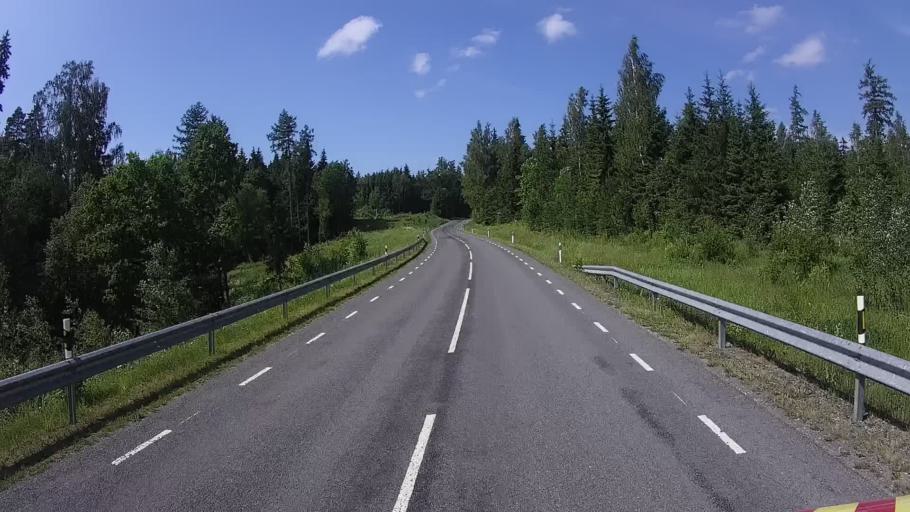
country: EE
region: Viljandimaa
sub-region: Karksi vald
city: Karksi-Nuia
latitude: 58.0818
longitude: 25.5596
